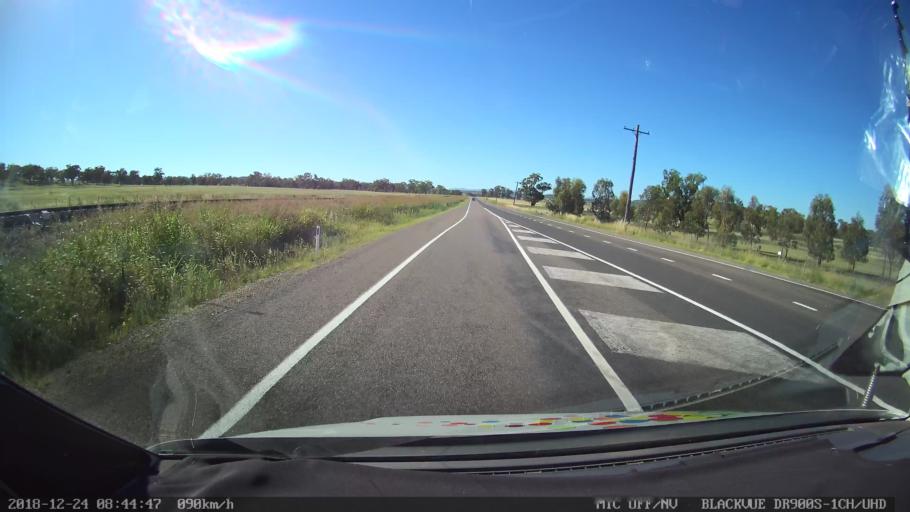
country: AU
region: New South Wales
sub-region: Liverpool Plains
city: Quirindi
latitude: -31.4063
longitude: 150.6496
